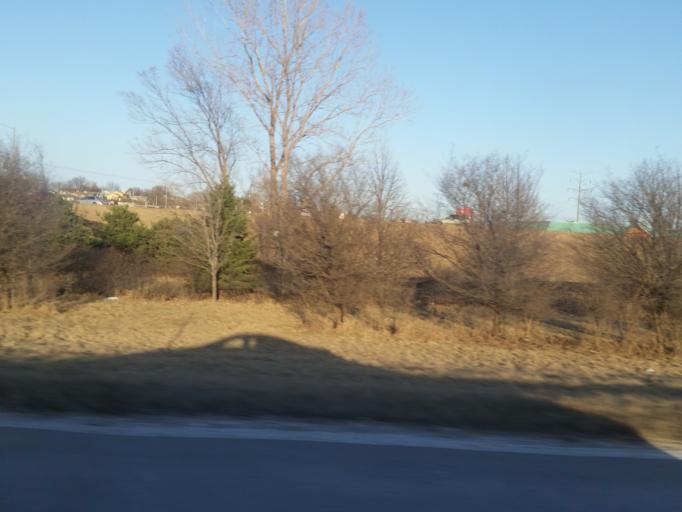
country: US
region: Nebraska
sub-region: Sarpy County
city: Offutt Air Force Base
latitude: 41.1582
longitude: -95.9387
